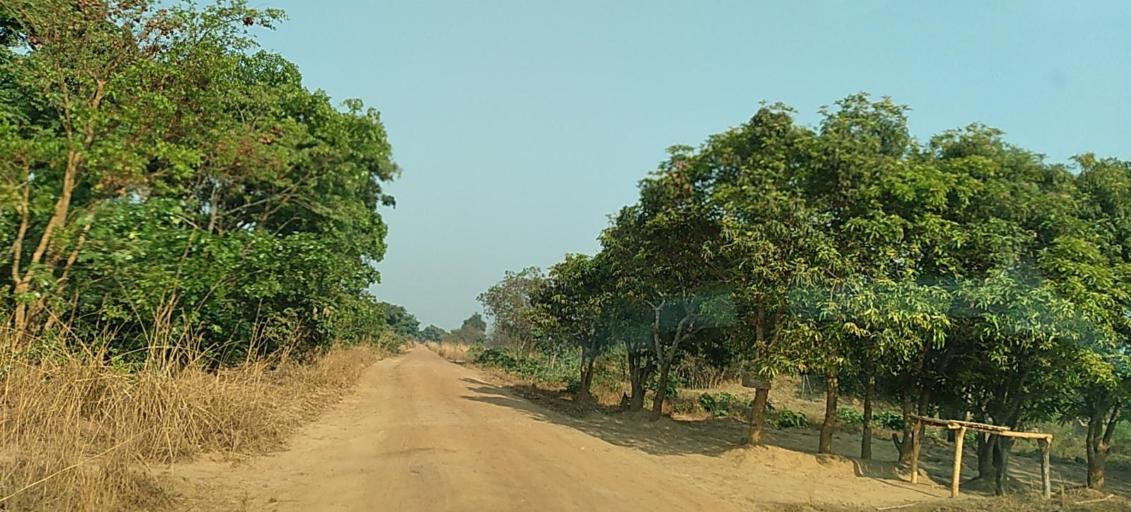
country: ZM
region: Copperbelt
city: Chingola
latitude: -12.8574
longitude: 27.5642
